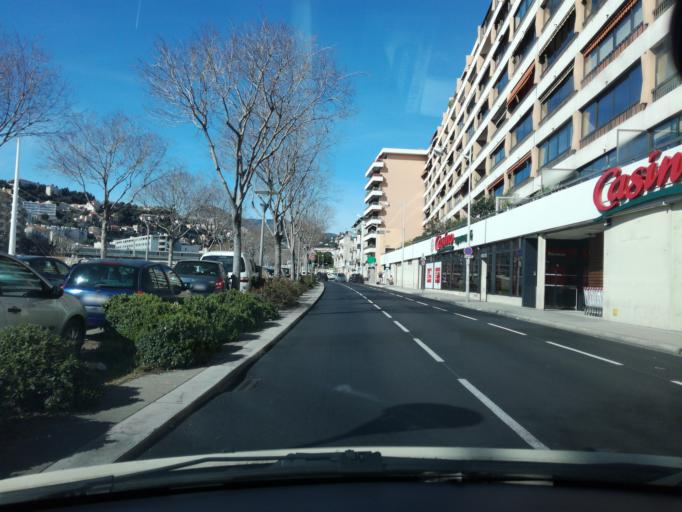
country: FR
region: Provence-Alpes-Cote d'Azur
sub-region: Departement des Alpes-Maritimes
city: Nice
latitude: 43.7119
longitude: 7.2842
